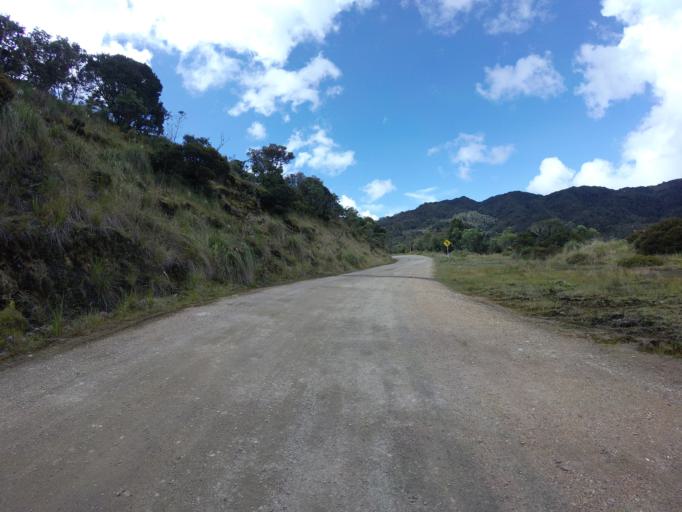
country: CO
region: Cundinamarca
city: Junin
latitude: 4.6285
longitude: -73.7240
